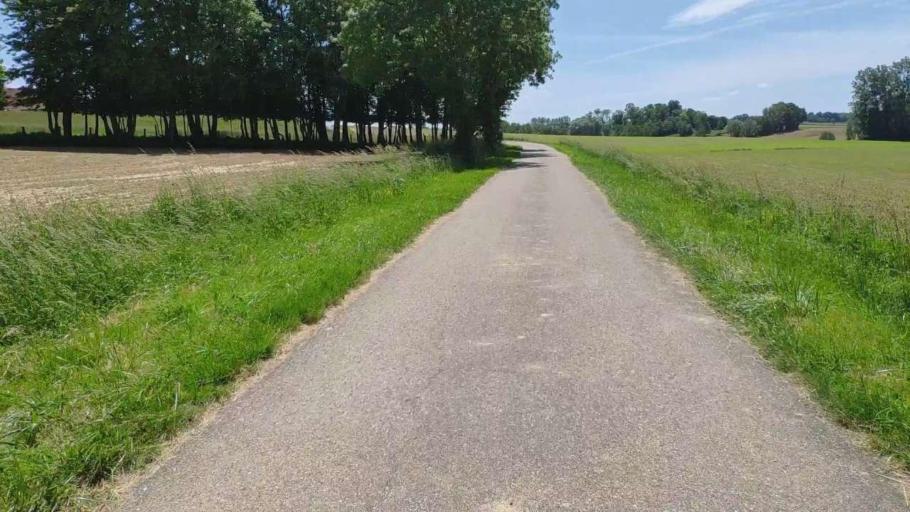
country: FR
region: Franche-Comte
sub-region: Departement du Jura
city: Bletterans
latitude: 46.8010
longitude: 5.3856
